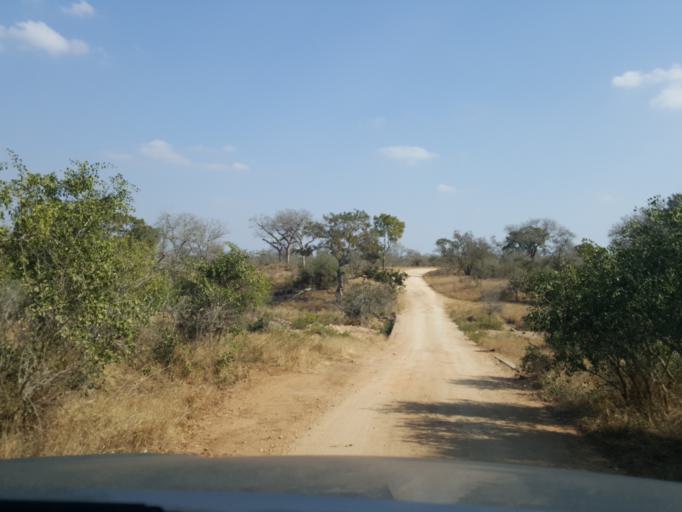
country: ZA
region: Mpumalanga
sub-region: Ehlanzeni District
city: Komatipoort
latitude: -25.2728
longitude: 31.7803
